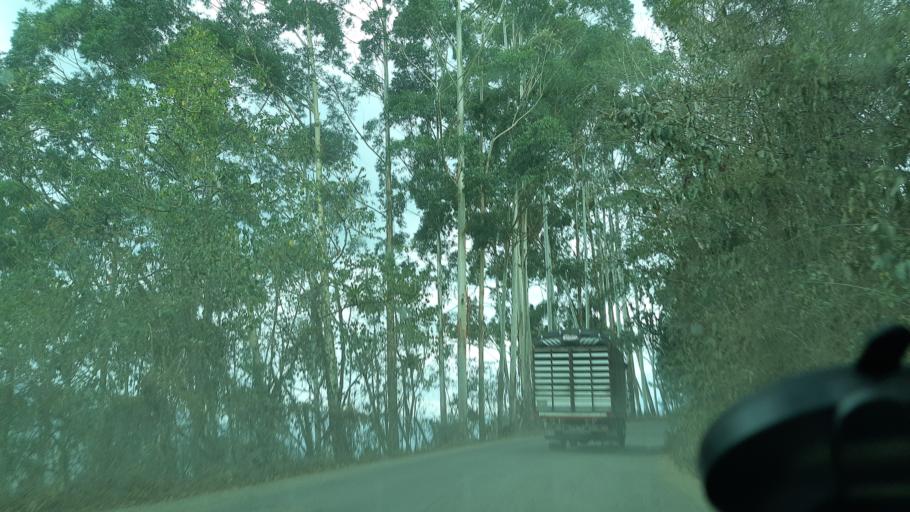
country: CO
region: Boyaca
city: Garagoa
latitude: 5.0770
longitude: -73.3727
